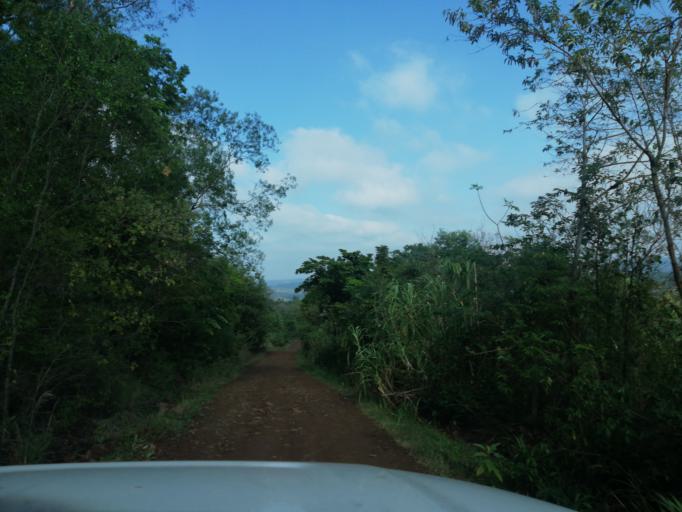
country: AR
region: Misiones
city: Cerro Azul
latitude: -27.5805
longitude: -55.5148
